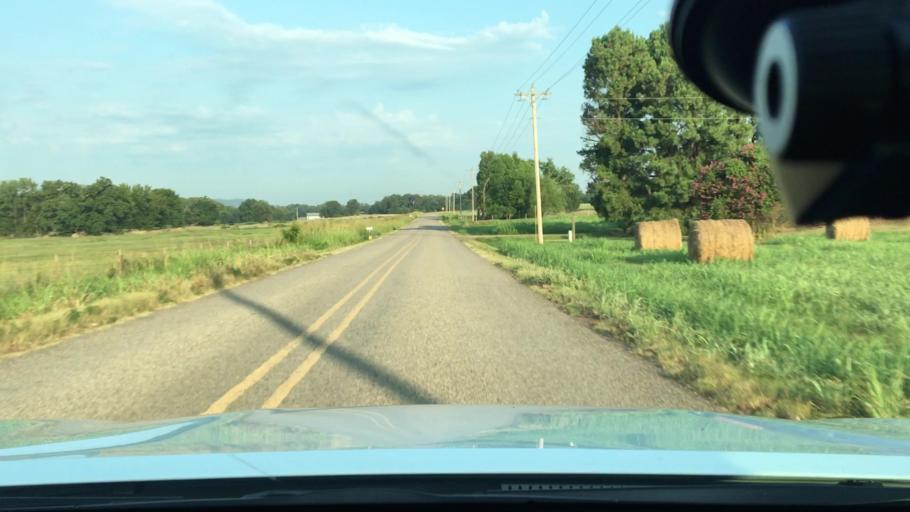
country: US
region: Arkansas
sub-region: Johnson County
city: Coal Hill
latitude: 35.3711
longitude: -93.5818
